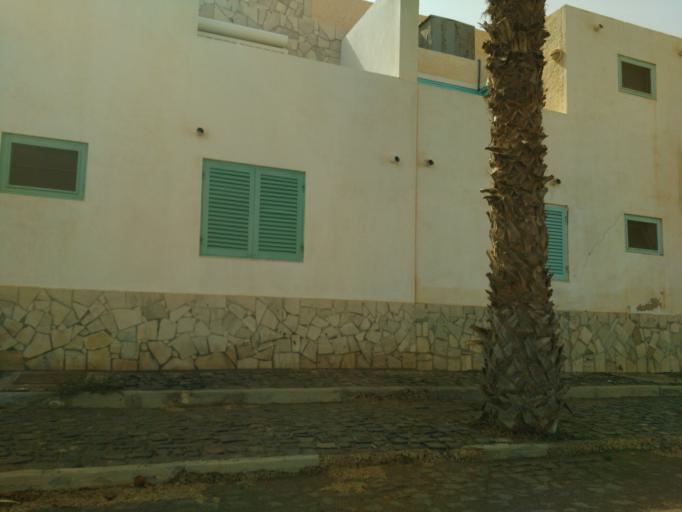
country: CV
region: Sal
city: Espargos
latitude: 16.6749
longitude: -22.9350
